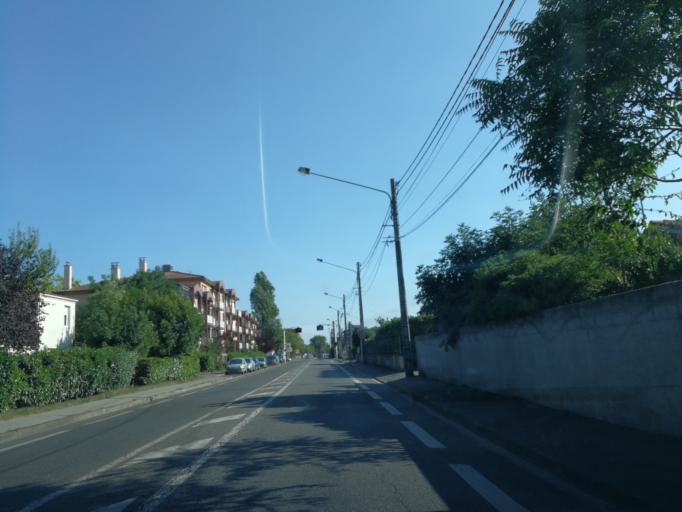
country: FR
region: Midi-Pyrenees
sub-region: Departement de la Haute-Garonne
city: Aucamville
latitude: 43.6420
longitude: 1.4391
